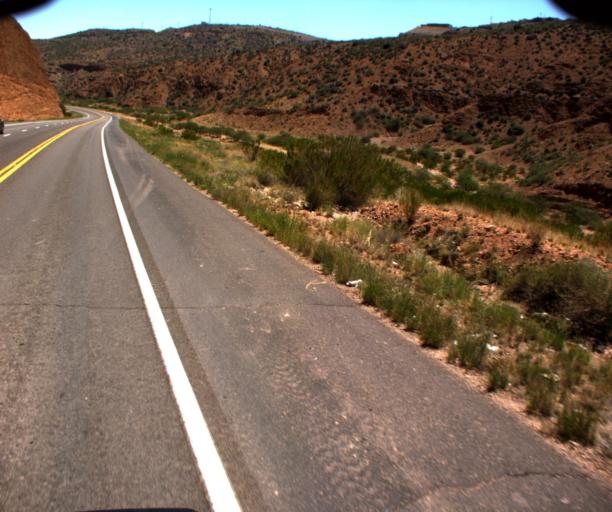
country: US
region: Arizona
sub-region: Greenlee County
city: Clifton
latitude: 33.0646
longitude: -109.3253
